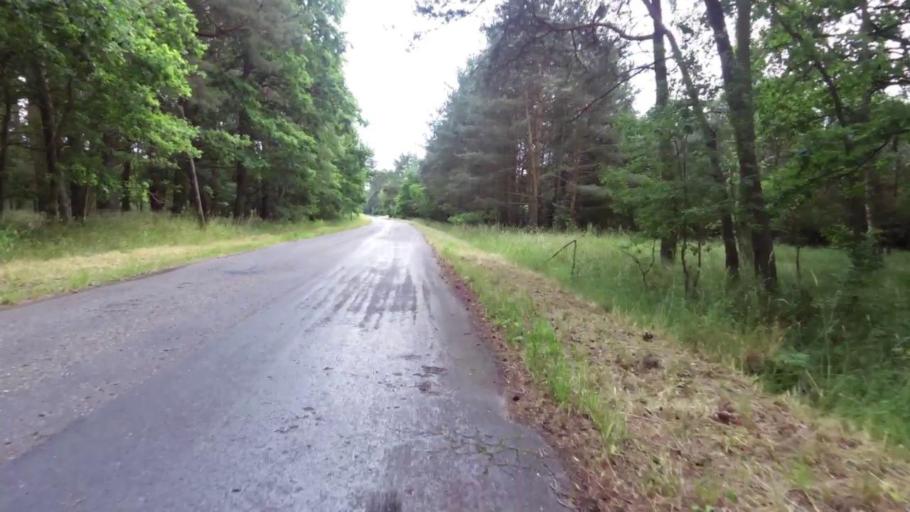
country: PL
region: West Pomeranian Voivodeship
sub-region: Powiat goleniowski
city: Stepnica
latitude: 53.7091
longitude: 14.5515
